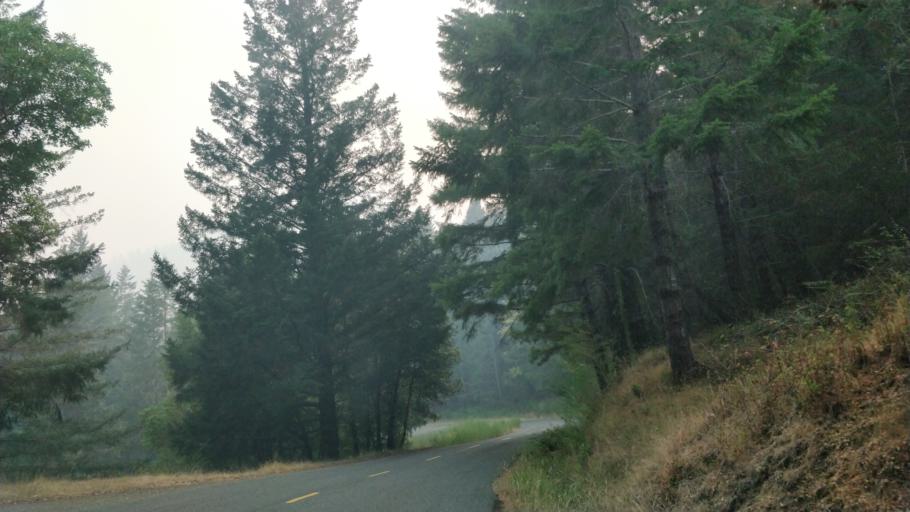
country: US
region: California
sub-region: Humboldt County
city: Rio Dell
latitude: 40.3265
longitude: -124.0427
